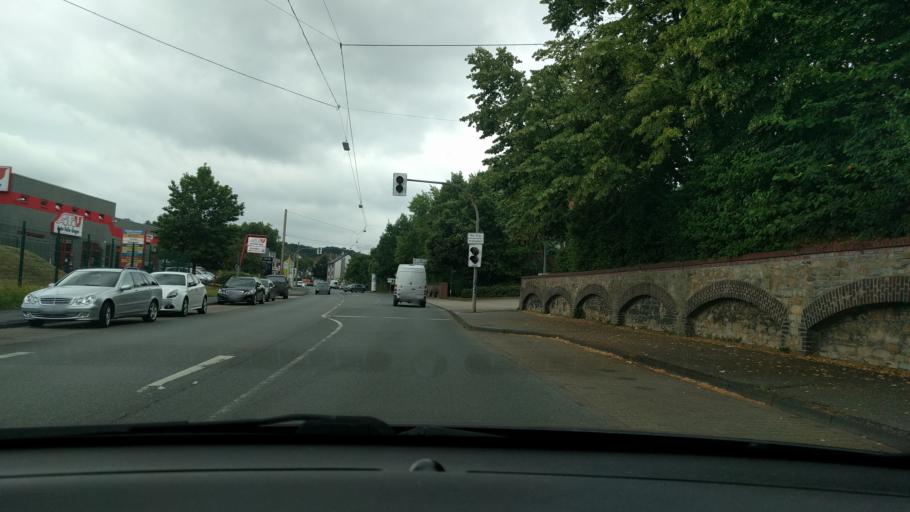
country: DE
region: North Rhine-Westphalia
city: Witten
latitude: 51.4409
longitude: 7.3508
